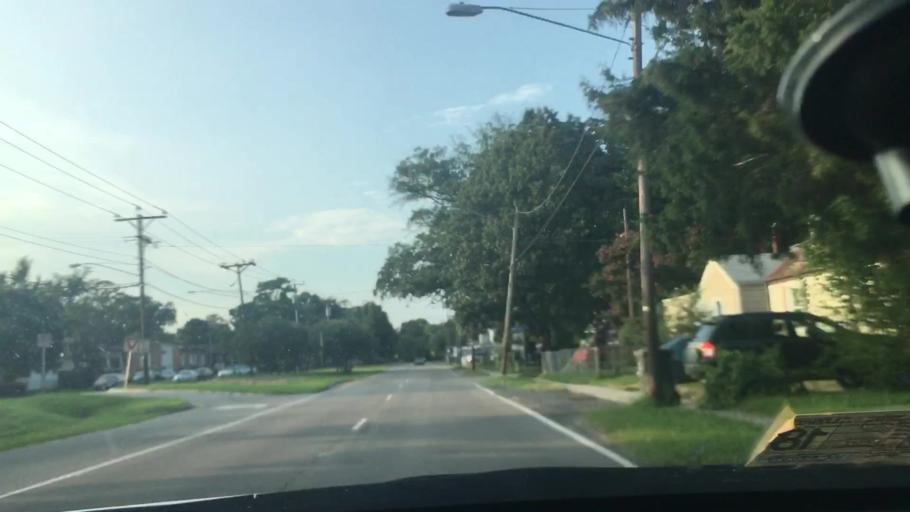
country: US
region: Virginia
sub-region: City of Norfolk
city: Norfolk
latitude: 36.9402
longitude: -76.2453
